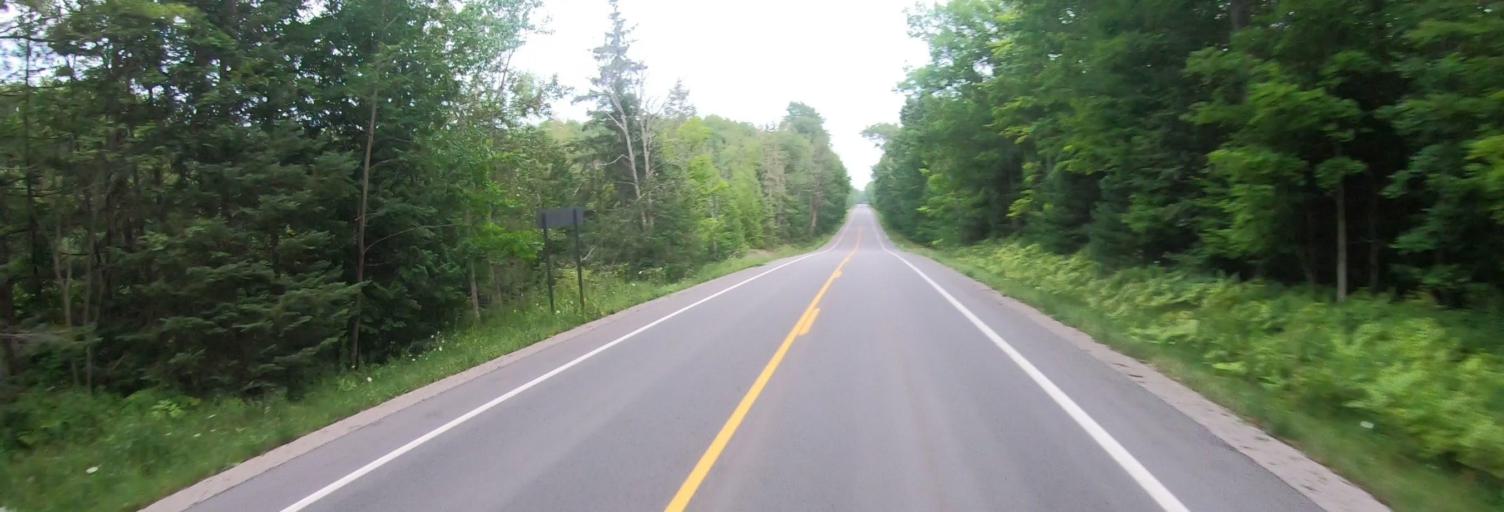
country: US
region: Michigan
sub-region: Mackinac County
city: Saint Ignace
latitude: 45.7752
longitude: -84.7732
